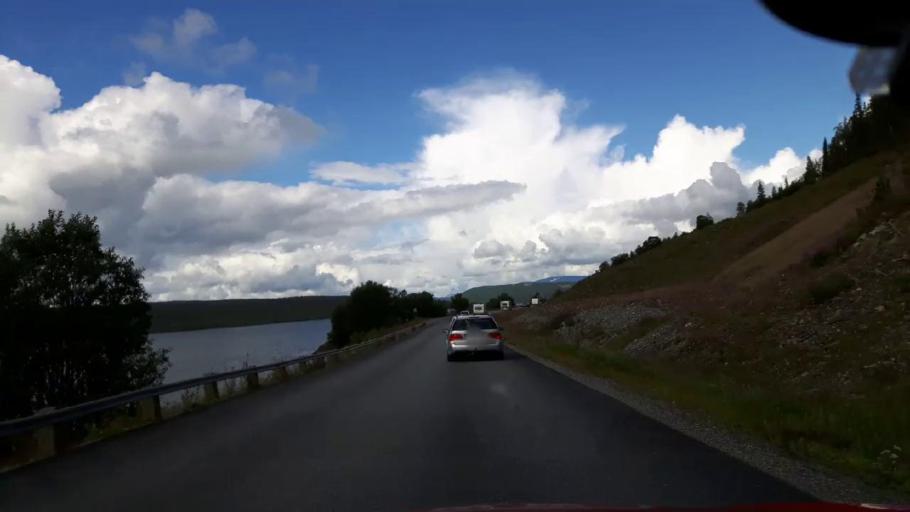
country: SE
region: Vaesterbotten
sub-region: Vilhelmina Kommun
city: Sjoberg
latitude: 65.0387
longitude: 15.1201
